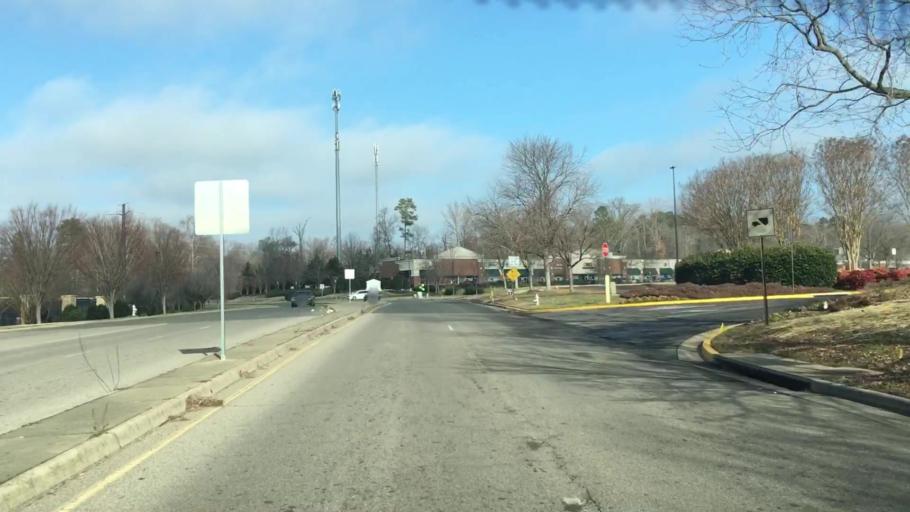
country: US
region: Virginia
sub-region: Chesterfield County
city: Bon Air
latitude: 37.5041
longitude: -77.6282
